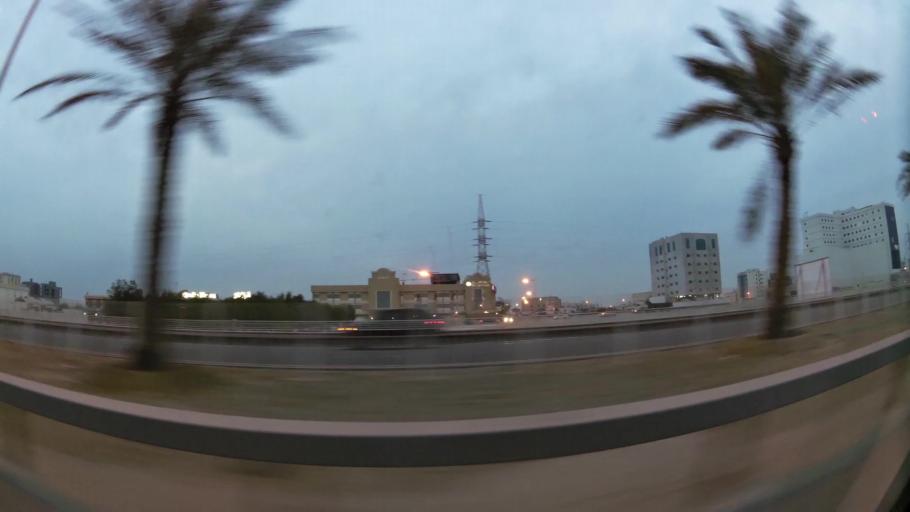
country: BH
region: Northern
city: Ar Rifa'
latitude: 26.1534
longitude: 50.5716
